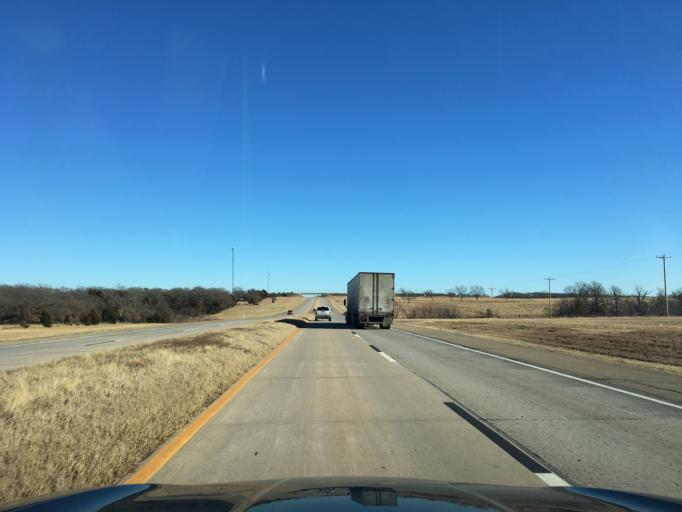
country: US
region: Oklahoma
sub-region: Pawnee County
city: Pawnee
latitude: 36.2245
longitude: -96.7598
